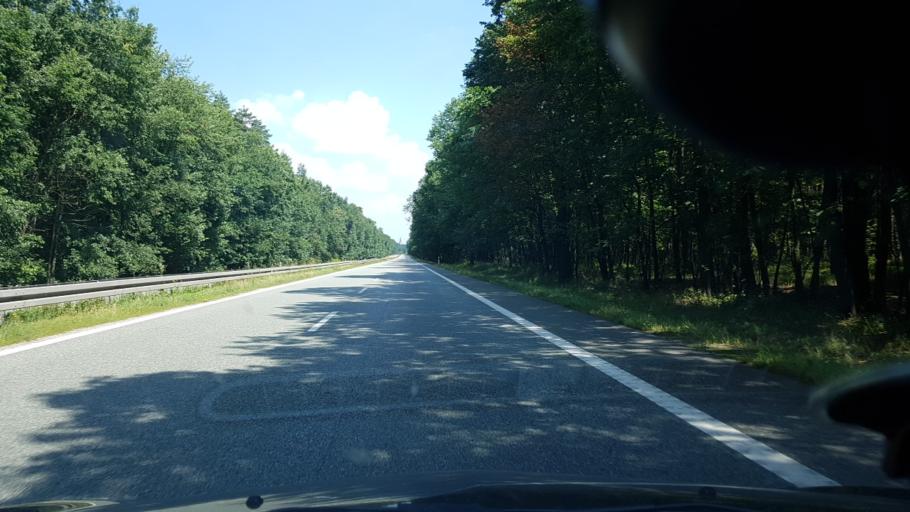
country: PL
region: Silesian Voivodeship
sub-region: Zory
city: Zory
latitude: 50.0690
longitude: 18.7346
